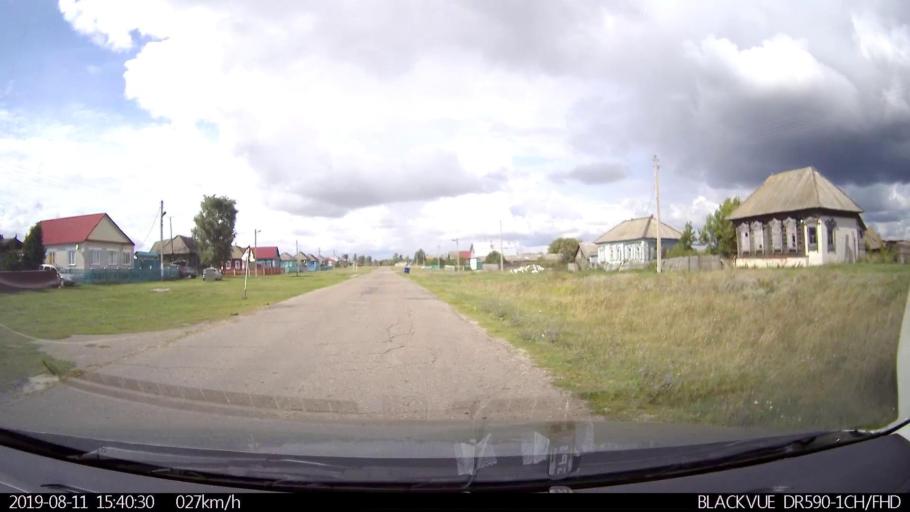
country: RU
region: Ulyanovsk
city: Ignatovka
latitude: 53.8696
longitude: 47.6501
